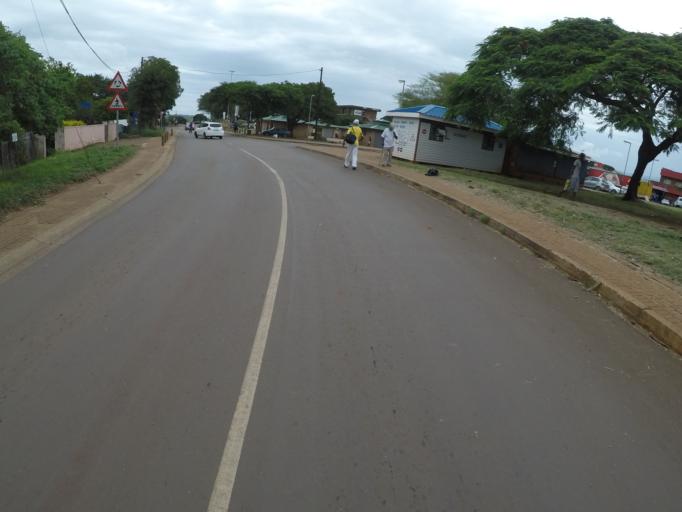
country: ZA
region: KwaZulu-Natal
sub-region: uThungulu District Municipality
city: Empangeni
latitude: -28.7729
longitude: 31.8633
